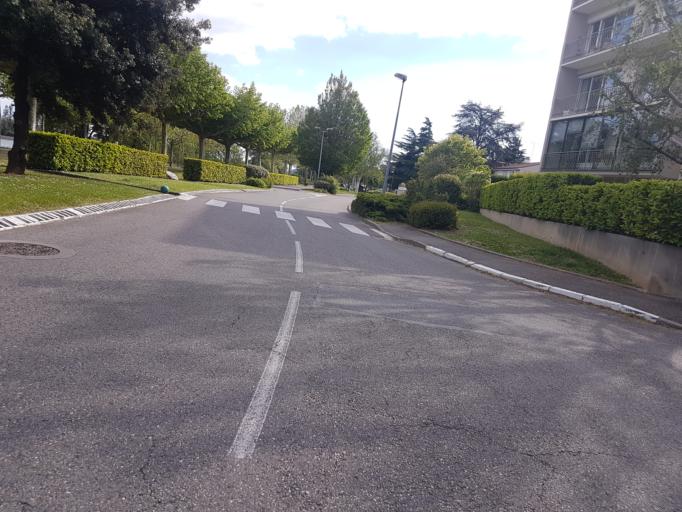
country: FR
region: Rhone-Alpes
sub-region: Departement de l'Ardeche
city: Guilherand-Granges
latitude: 44.9287
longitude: 4.8772
